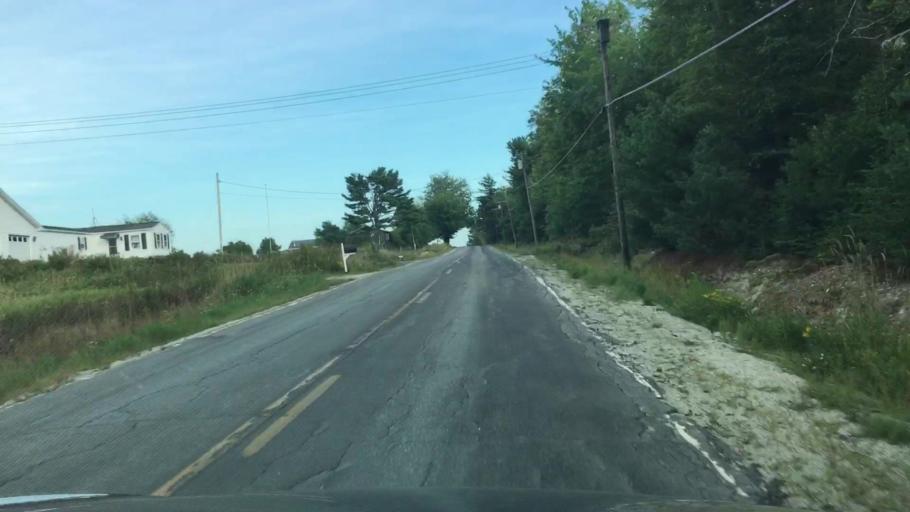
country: US
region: Maine
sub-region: Hancock County
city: Surry
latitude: 44.5051
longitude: -68.5892
